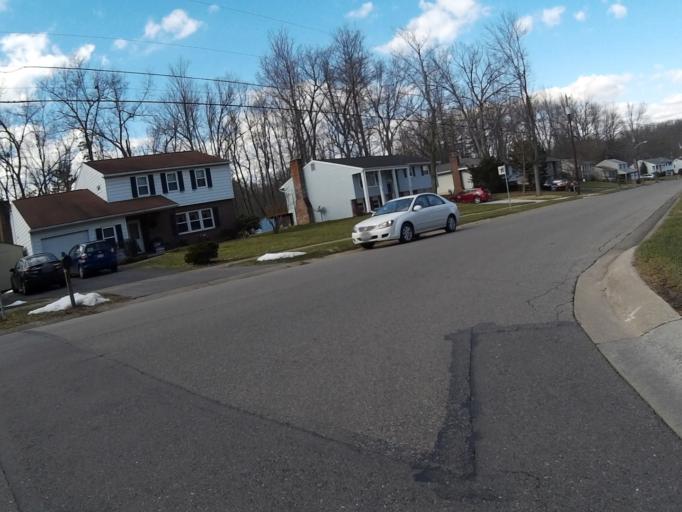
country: US
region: Pennsylvania
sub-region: Centre County
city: Park Forest Village
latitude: 40.8021
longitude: -77.9204
